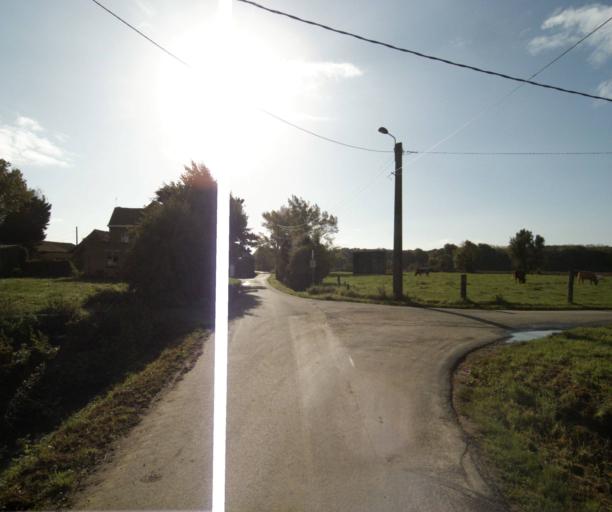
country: FR
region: Nord-Pas-de-Calais
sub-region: Departement du Nord
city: Verlinghem
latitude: 50.6891
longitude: 2.9851
